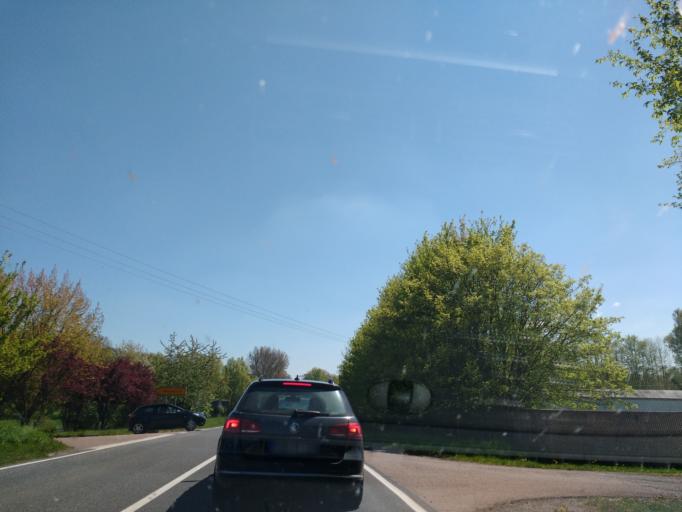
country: DE
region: Saxony-Anhalt
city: Deuben
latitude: 51.1200
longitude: 12.0721
